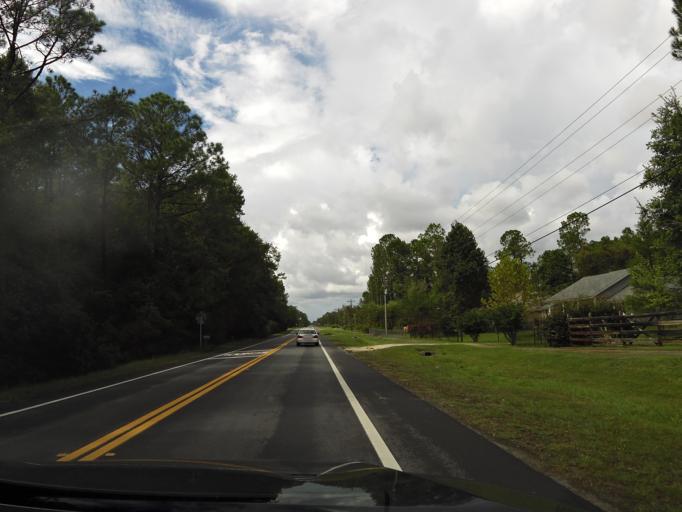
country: US
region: Florida
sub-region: Duval County
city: Baldwin
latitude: 30.1462
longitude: -82.0111
